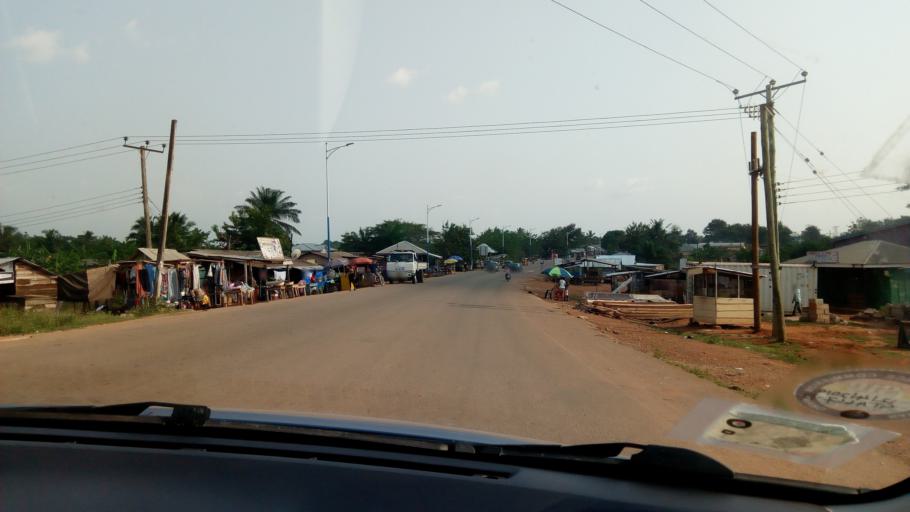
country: GH
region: Western
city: Bibiani
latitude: 6.7979
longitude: -2.5180
